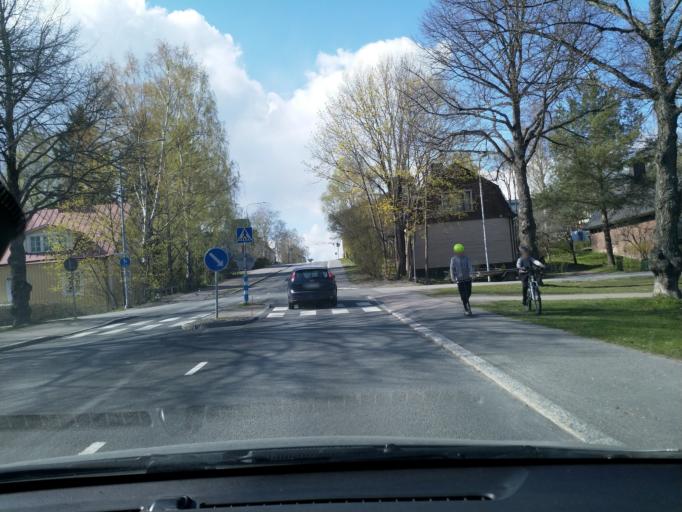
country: FI
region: Pirkanmaa
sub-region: Tampere
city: Tampere
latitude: 61.4847
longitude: 23.7870
